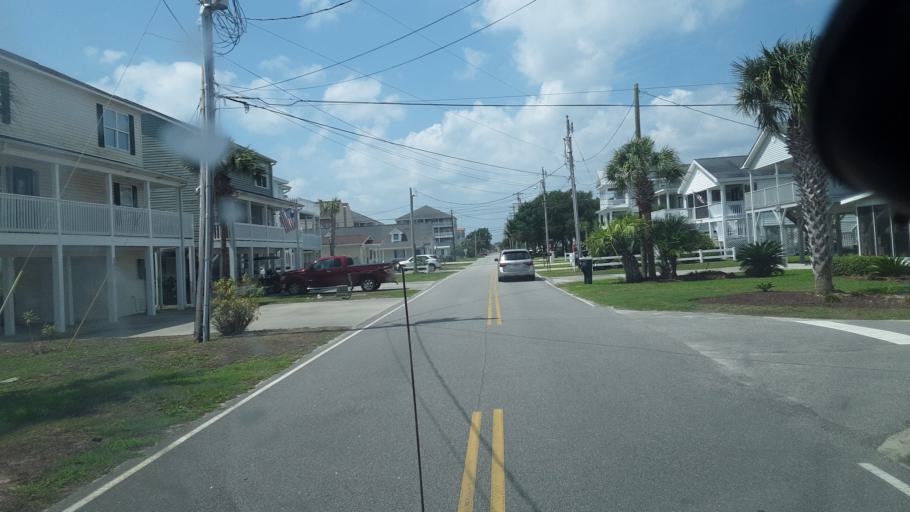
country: US
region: South Carolina
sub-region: Horry County
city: North Myrtle Beach
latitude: 33.8310
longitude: -78.6370
